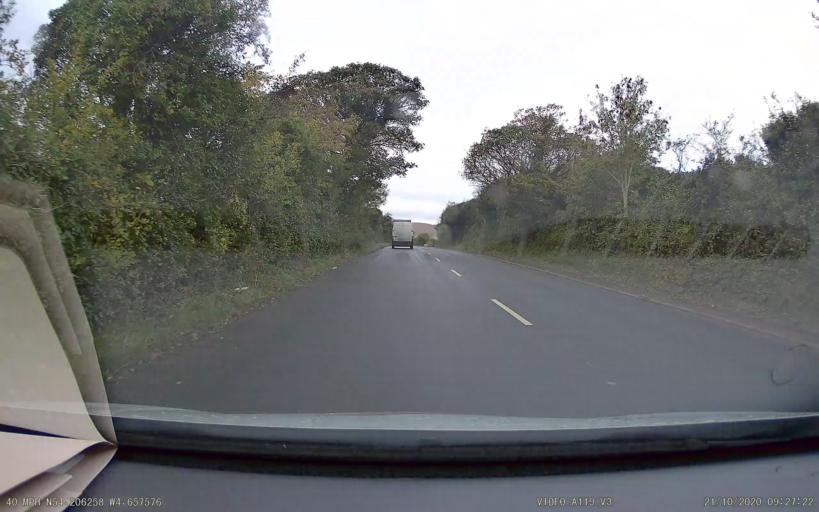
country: IM
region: Castletown
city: Castletown
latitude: 54.2063
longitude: -4.6576
